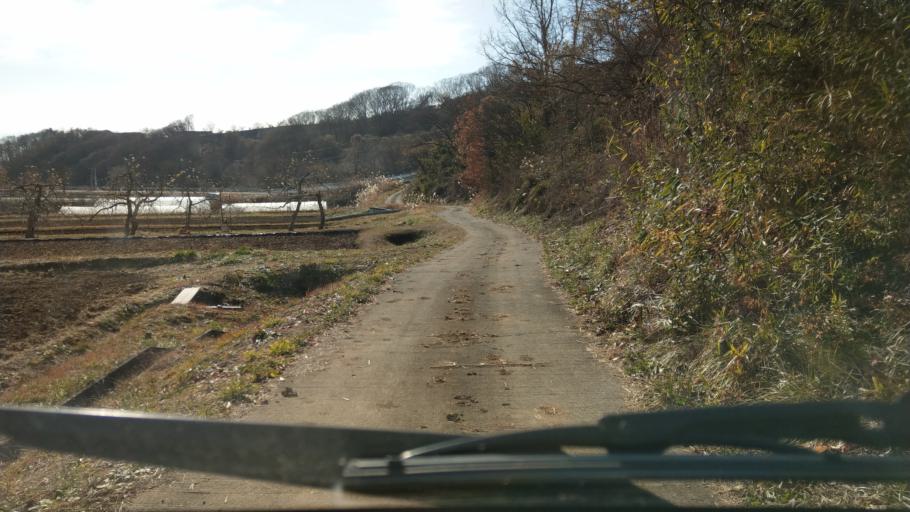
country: JP
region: Nagano
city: Komoro
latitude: 36.3461
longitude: 138.4222
